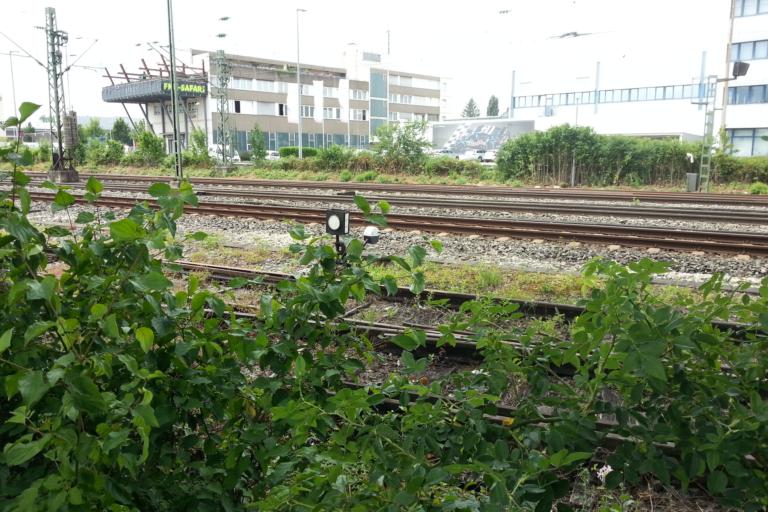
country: DE
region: Baden-Wuerttemberg
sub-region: Regierungsbezirk Stuttgart
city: Fellbach
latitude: 48.8185
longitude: 9.2654
